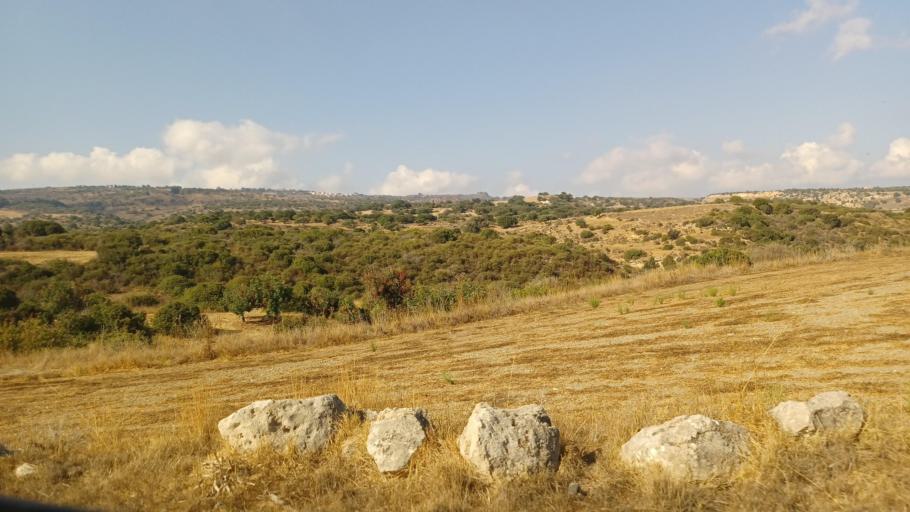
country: CY
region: Pafos
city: Polis
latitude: 34.9795
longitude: 32.4309
